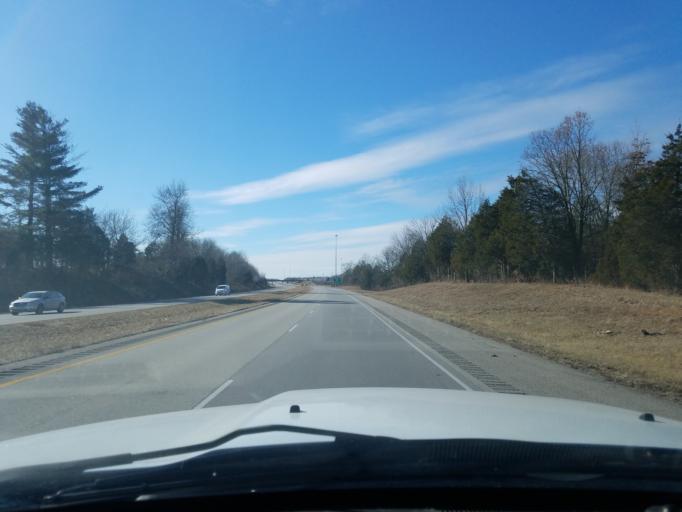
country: US
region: Kentucky
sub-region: Grayson County
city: Leitchfield
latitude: 37.4922
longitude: -86.2001
